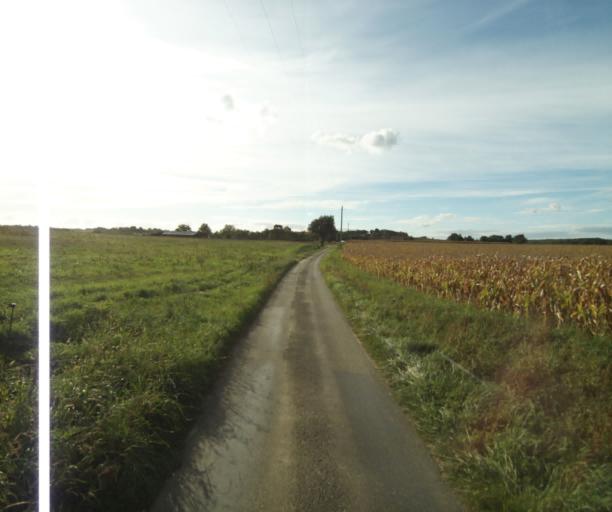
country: FR
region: Midi-Pyrenees
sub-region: Departement du Gers
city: Gondrin
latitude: 43.8905
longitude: 0.2879
